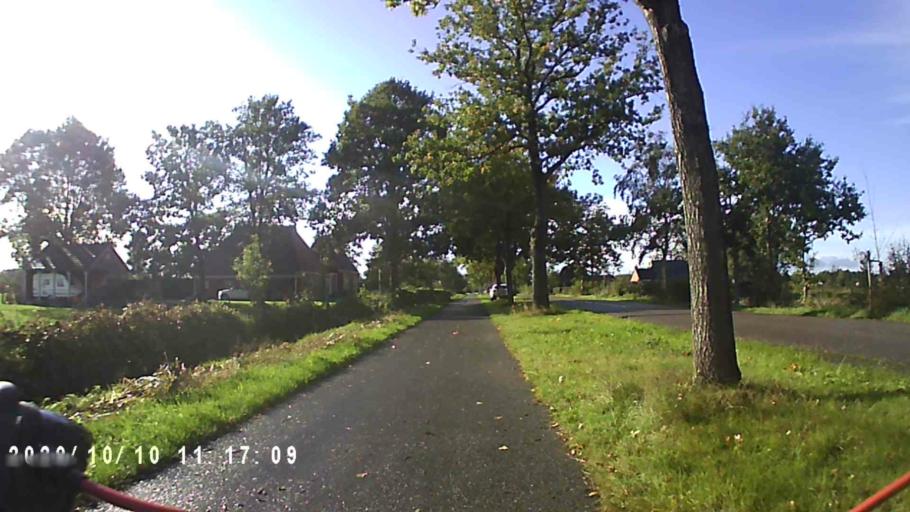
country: NL
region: Friesland
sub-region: Gemeente Smallingerland
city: Drachtstercompagnie
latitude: 53.0973
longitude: 6.1985
